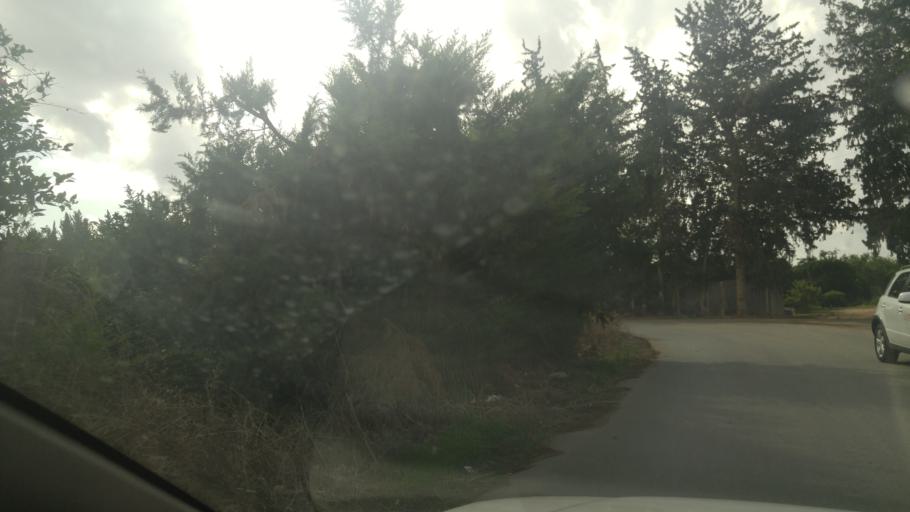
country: CY
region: Pafos
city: Paphos
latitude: 34.7442
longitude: 32.4816
